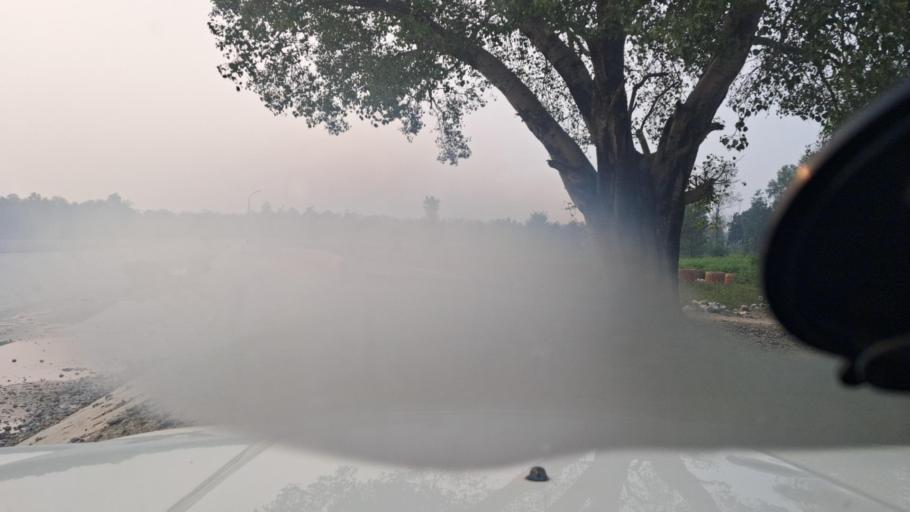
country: IN
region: Uttarakhand
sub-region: Udham Singh Nagar
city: Tanakpur
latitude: 29.0510
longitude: 80.1339
